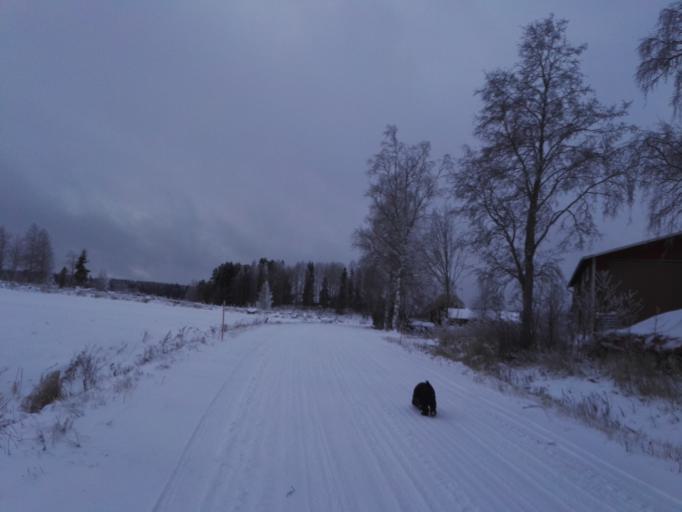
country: FI
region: Satakunta
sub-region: Pohjois-Satakunta
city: Jaemijaervi
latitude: 61.7824
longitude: 22.8777
